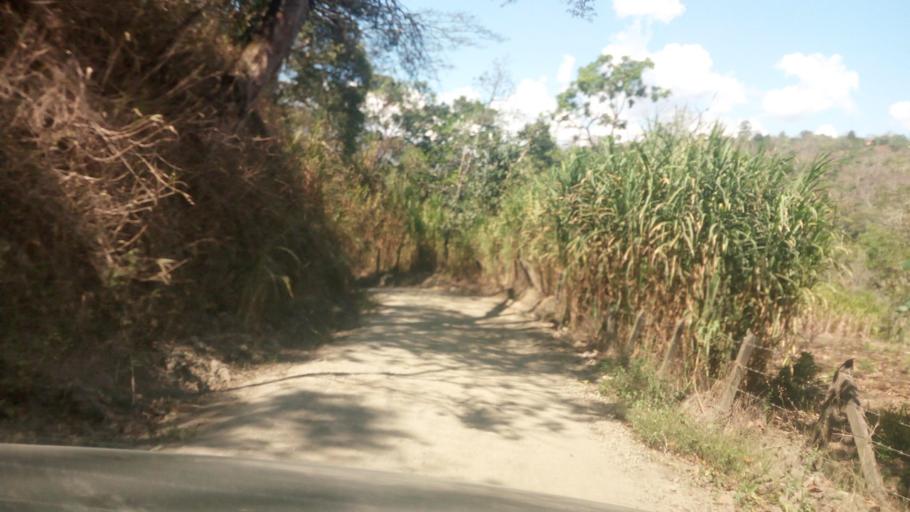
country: CO
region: Boyaca
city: Somondoco
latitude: 4.9858
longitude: -73.4465
